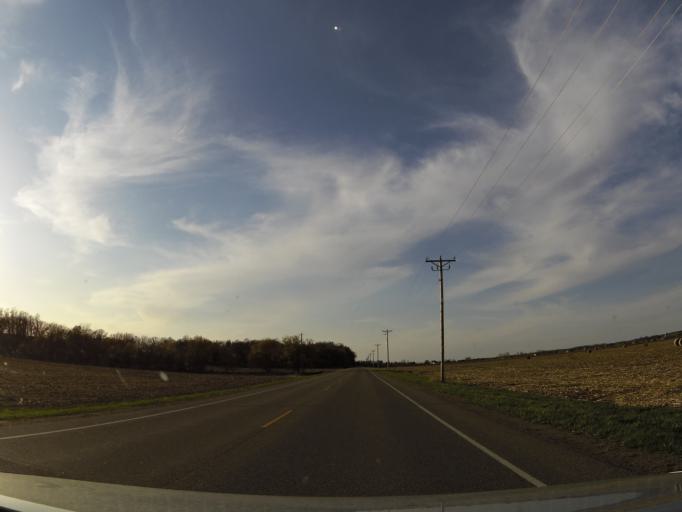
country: US
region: Wisconsin
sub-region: Pierce County
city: River Falls
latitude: 44.9032
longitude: -92.6760
